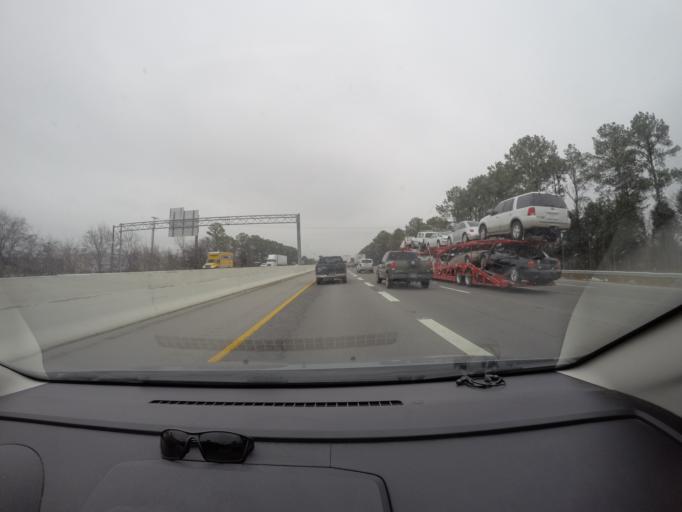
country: US
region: Tennessee
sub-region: Rutherford County
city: Murfreesboro
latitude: 35.8606
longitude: -86.4499
